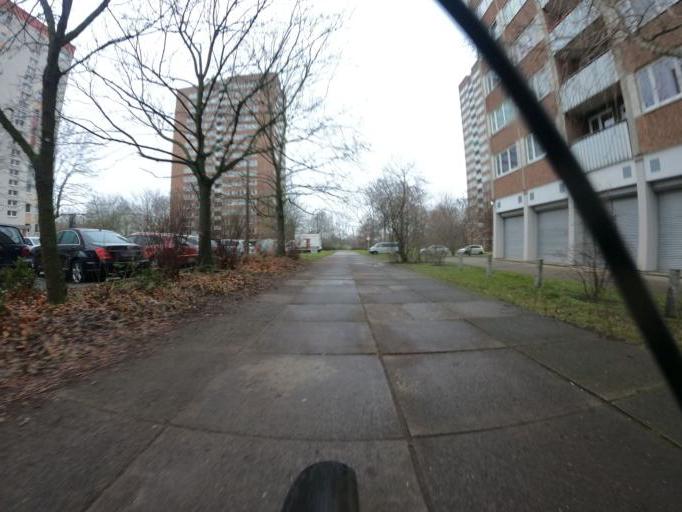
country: DE
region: Berlin
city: Marzahn
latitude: 52.5506
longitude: 13.5590
